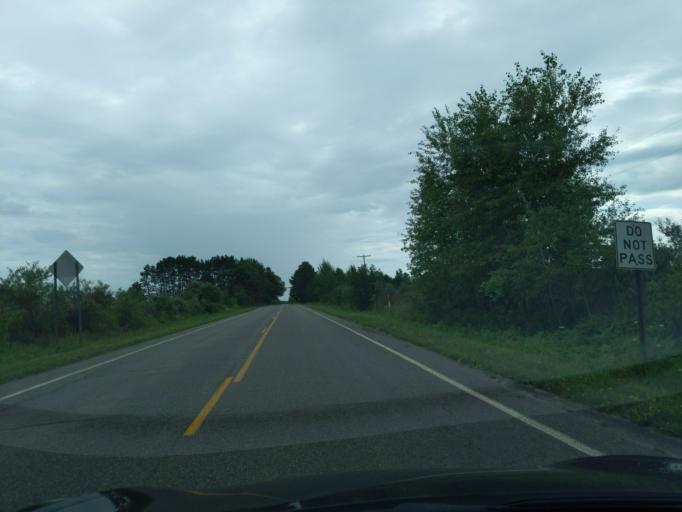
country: US
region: Michigan
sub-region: Clare County
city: Harrison
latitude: 44.0292
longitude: -84.9494
